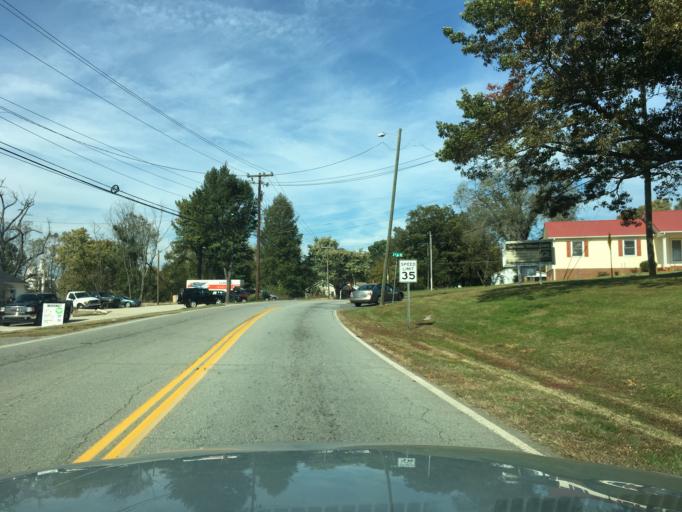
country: US
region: North Carolina
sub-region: Catawba County
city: Hickory
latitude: 35.7280
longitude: -81.2987
